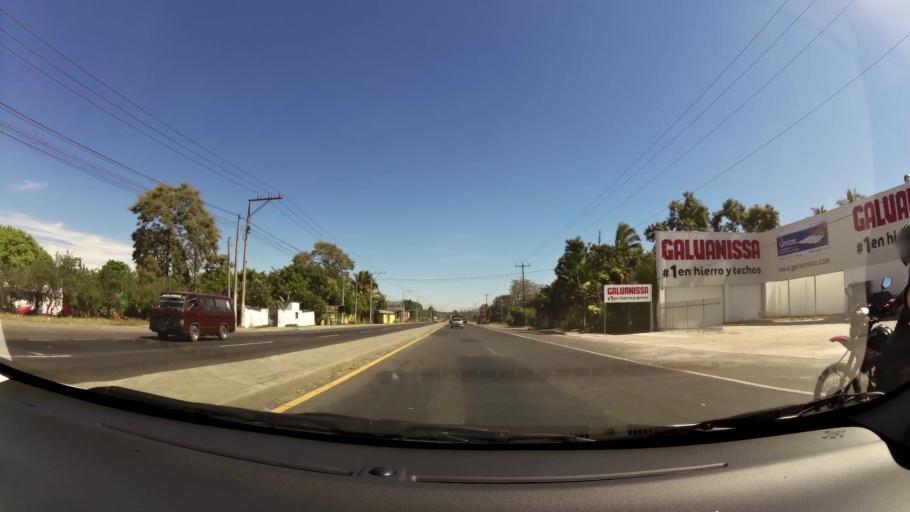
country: SV
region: La Libertad
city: San Juan Opico
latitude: 13.7826
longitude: -89.3675
